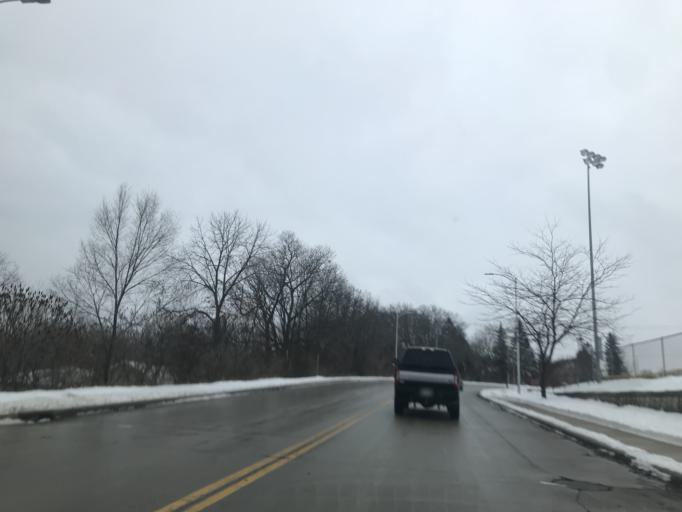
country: US
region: Wisconsin
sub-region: Door County
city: Sturgeon Bay
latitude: 44.8258
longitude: -87.3845
